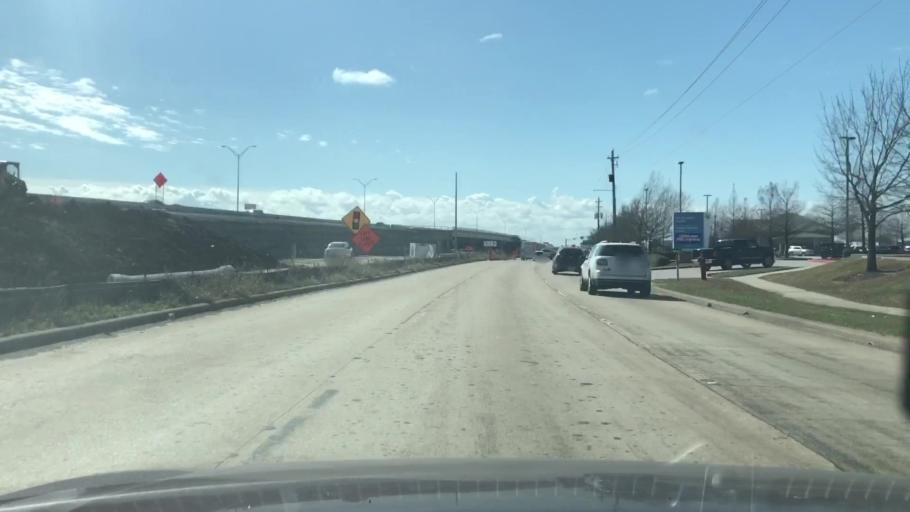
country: US
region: Texas
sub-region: Harris County
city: Pasadena
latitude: 29.6415
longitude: -95.1597
